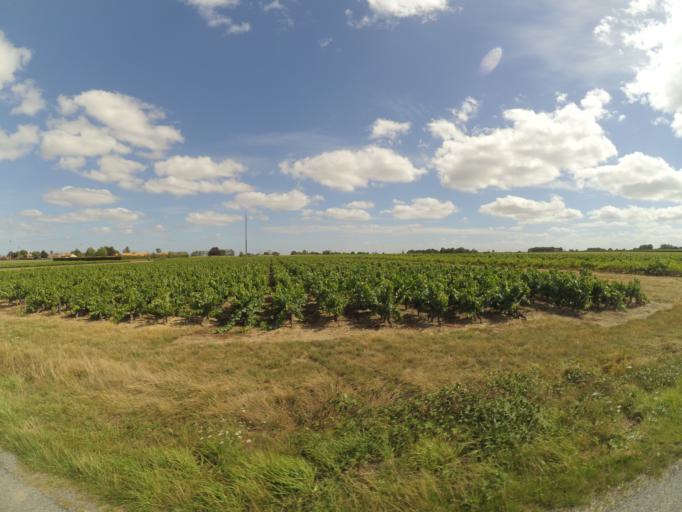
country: FR
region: Pays de la Loire
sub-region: Departement de la Loire-Atlantique
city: Remouille
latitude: 47.0528
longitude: -1.3860
